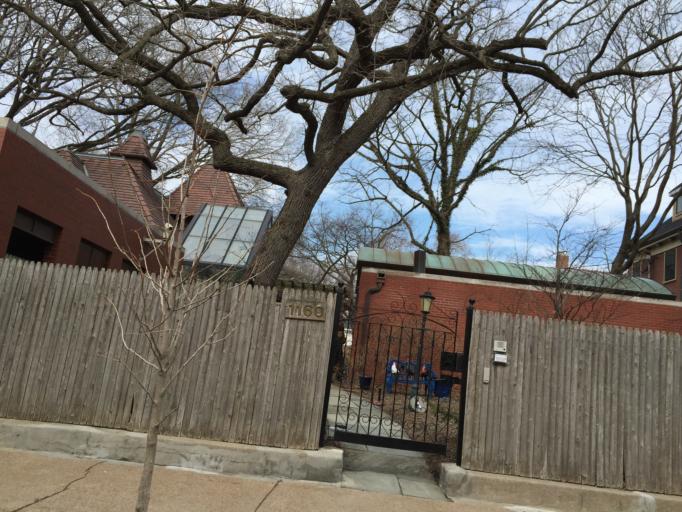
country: US
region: Illinois
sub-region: Cook County
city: Chicago
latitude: 41.7933
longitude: -87.5972
